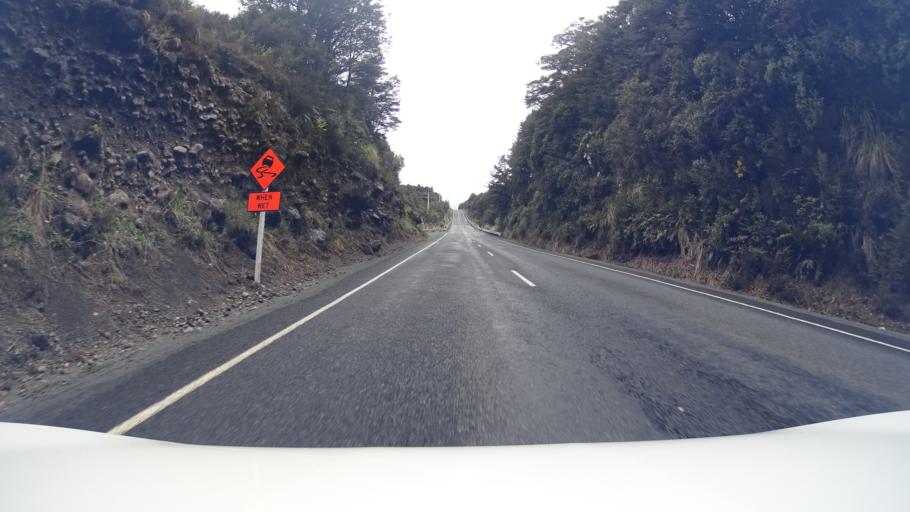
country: NZ
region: Manawatu-Wanganui
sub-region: Ruapehu District
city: Waiouru
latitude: -39.1761
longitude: 175.4709
